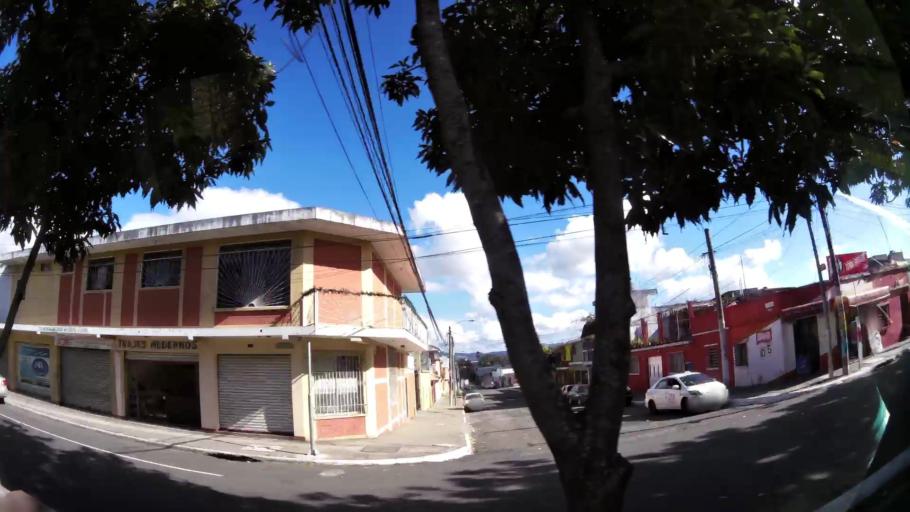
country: GT
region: Guatemala
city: Guatemala City
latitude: 14.6163
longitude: -90.5507
